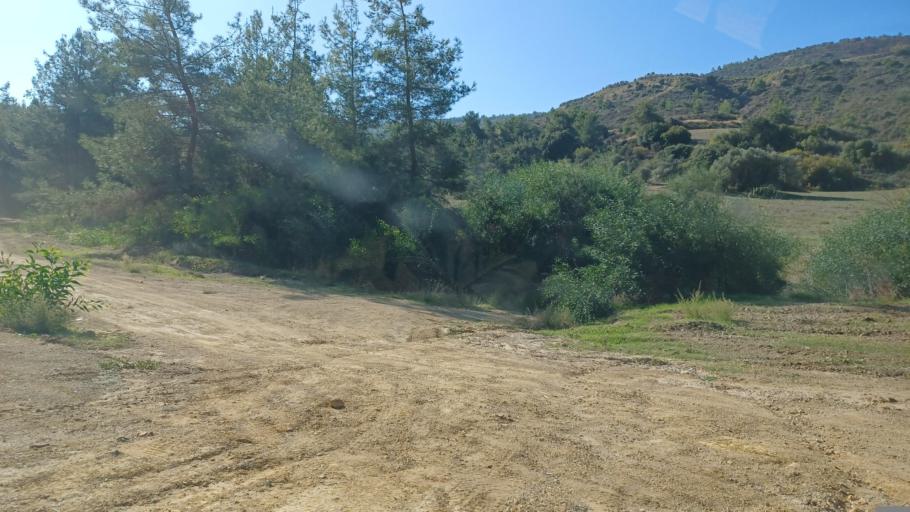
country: CY
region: Pafos
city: Polis
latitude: 35.0289
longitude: 32.4899
